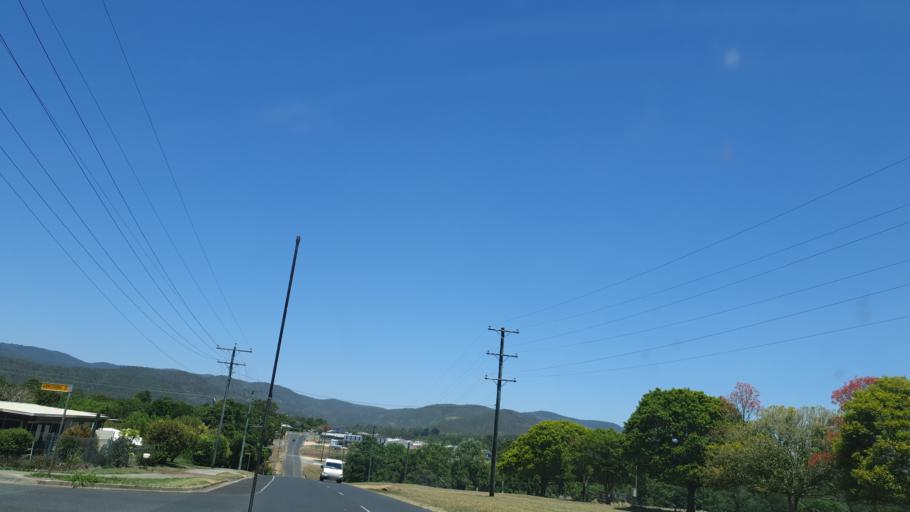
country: AU
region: Queensland
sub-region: Tablelands
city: Atherton
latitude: -17.2574
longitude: 145.4823
